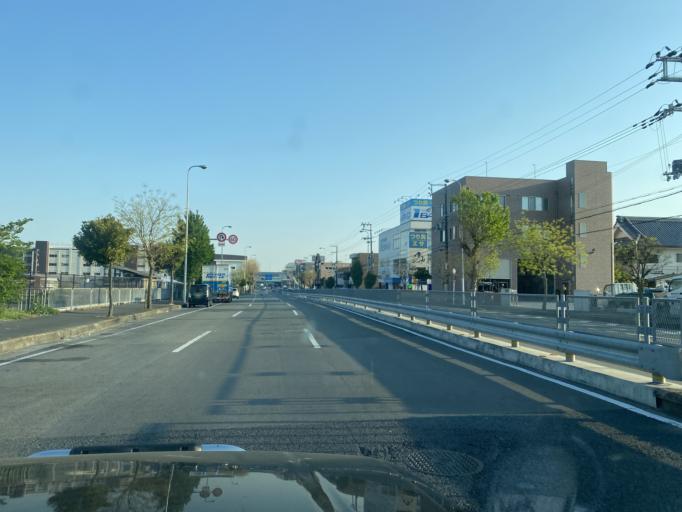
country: JP
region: Osaka
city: Ikeda
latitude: 34.8103
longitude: 135.4316
